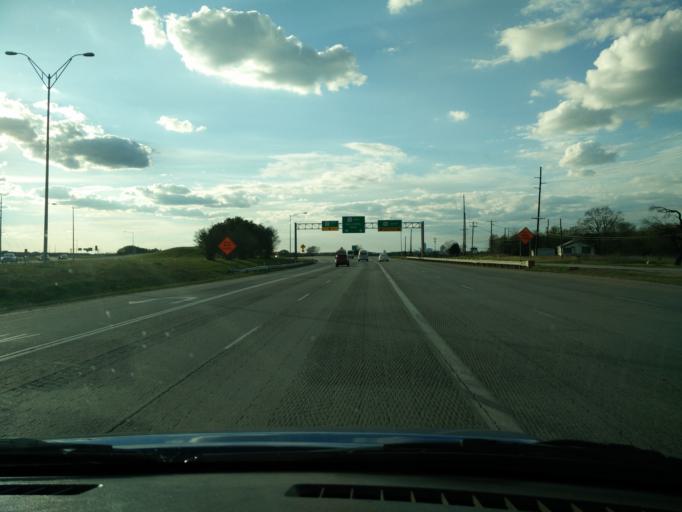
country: US
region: Texas
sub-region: Travis County
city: Austin
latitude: 30.2224
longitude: -97.6765
